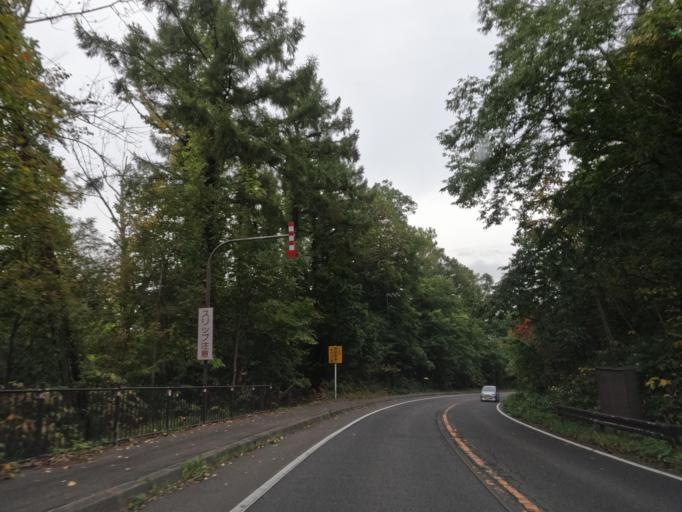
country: JP
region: Hokkaido
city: Date
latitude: 42.5373
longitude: 140.8608
